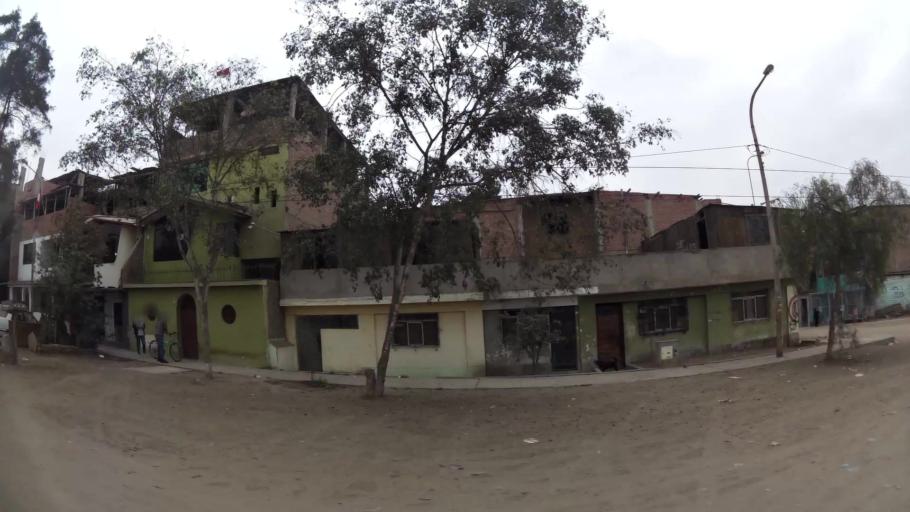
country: PE
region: Lima
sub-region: Lima
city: Surco
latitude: -12.2042
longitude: -76.9356
